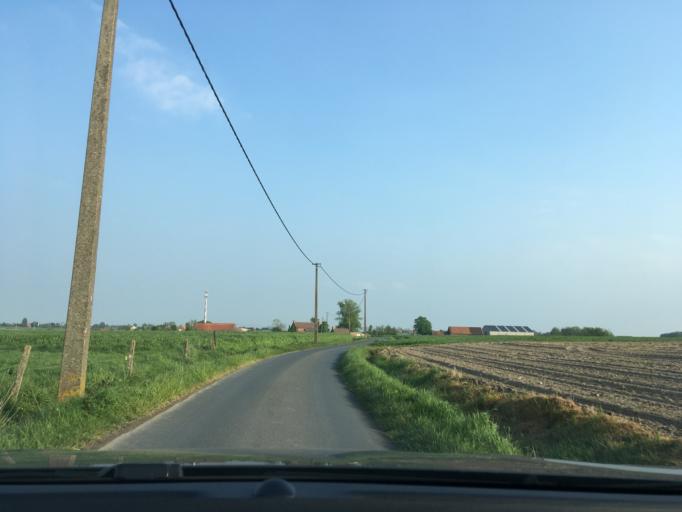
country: BE
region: Flanders
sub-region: Provincie West-Vlaanderen
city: Lichtervelde
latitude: 51.0124
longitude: 3.1587
